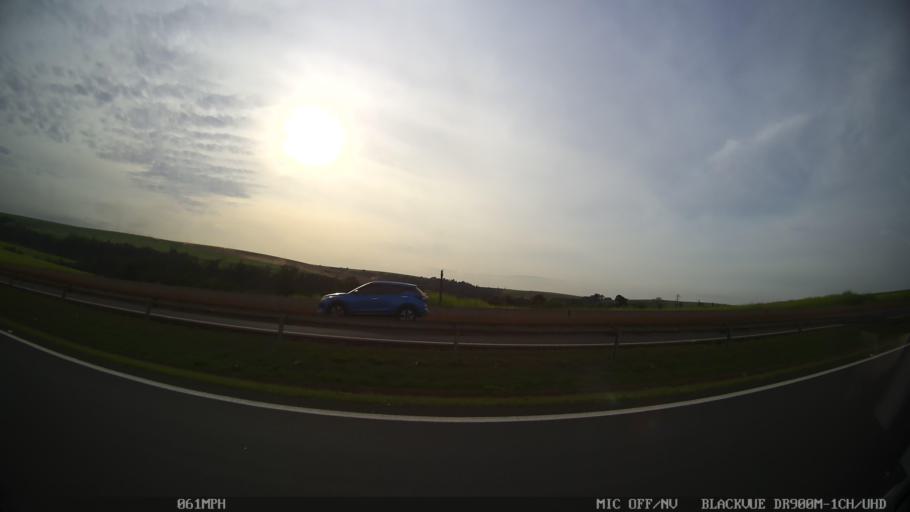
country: BR
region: Sao Paulo
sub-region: Piracicaba
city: Piracicaba
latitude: -22.6810
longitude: -47.5687
